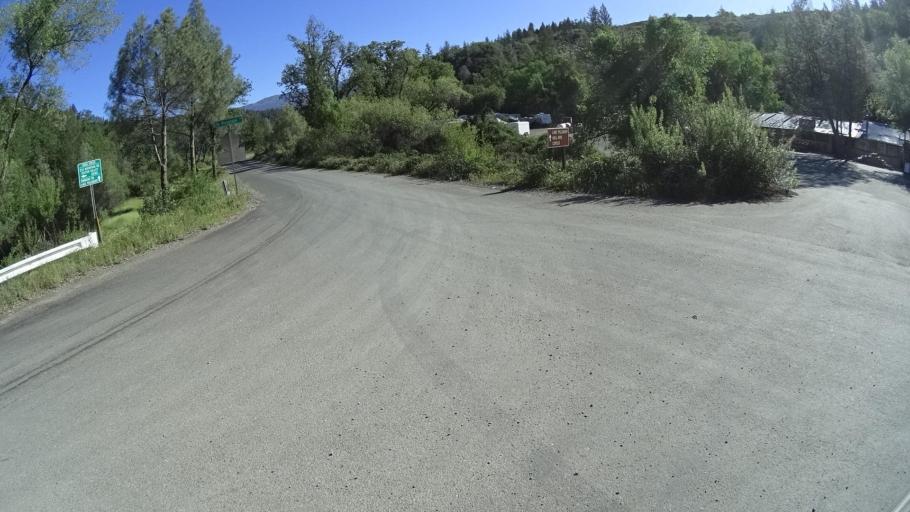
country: US
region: California
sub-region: Lake County
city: Upper Lake
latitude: 39.4199
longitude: -122.9790
